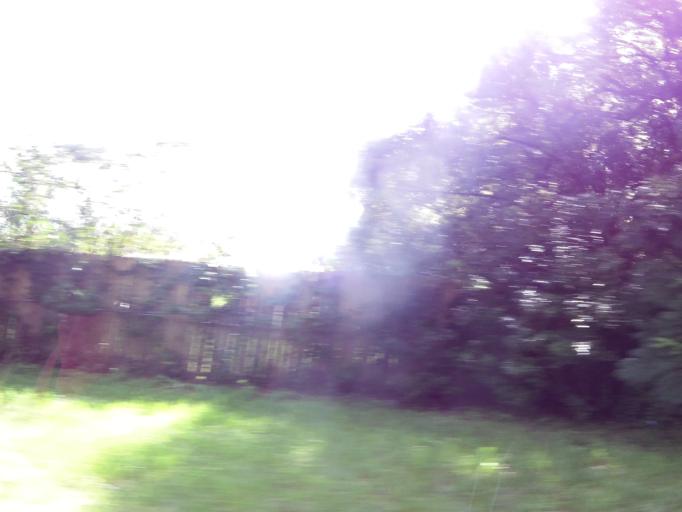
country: US
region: Florida
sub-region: Clay County
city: Green Cove Springs
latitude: 29.9829
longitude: -81.6950
